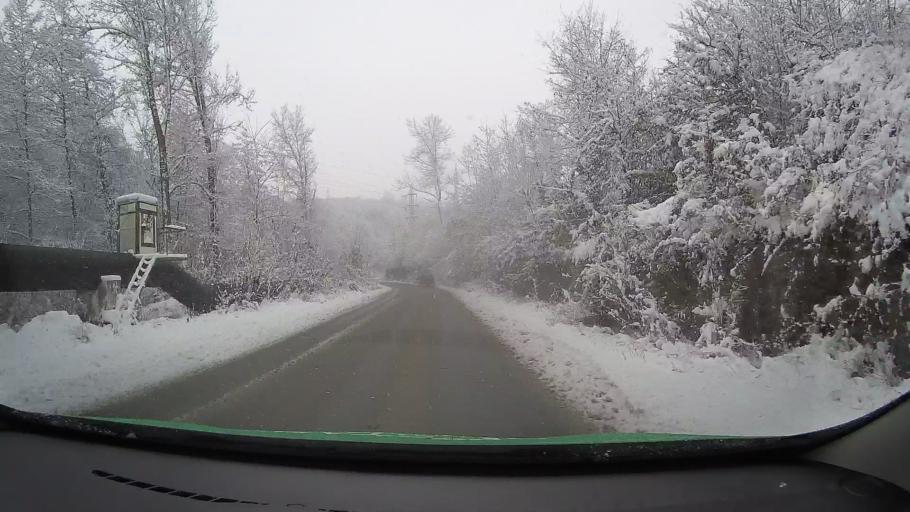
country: RO
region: Hunedoara
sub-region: Comuna Teliucu Inferior
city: Teliucu Inferior
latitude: 45.7316
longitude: 22.8810
